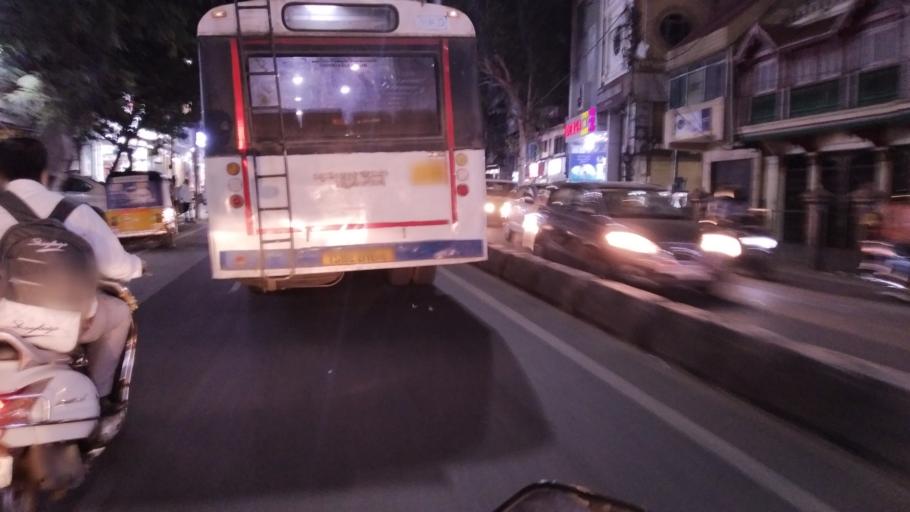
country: IN
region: Telangana
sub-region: Hyderabad
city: Malkajgiri
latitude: 17.4375
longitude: 78.4886
